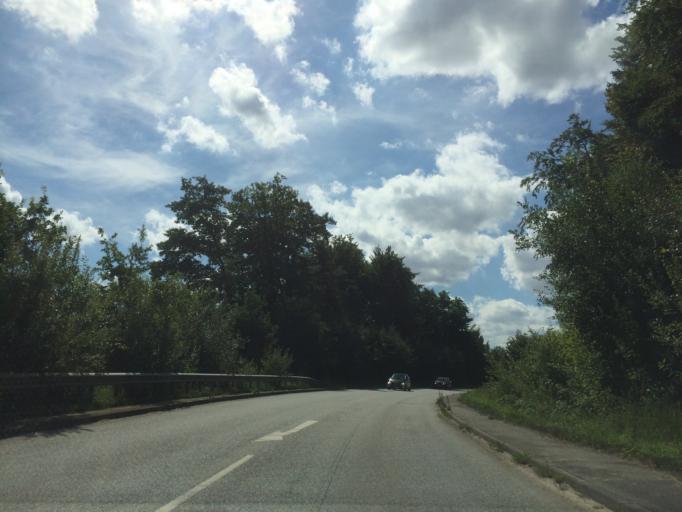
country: DE
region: Schleswig-Holstein
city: Eutin
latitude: 54.1496
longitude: 10.6014
